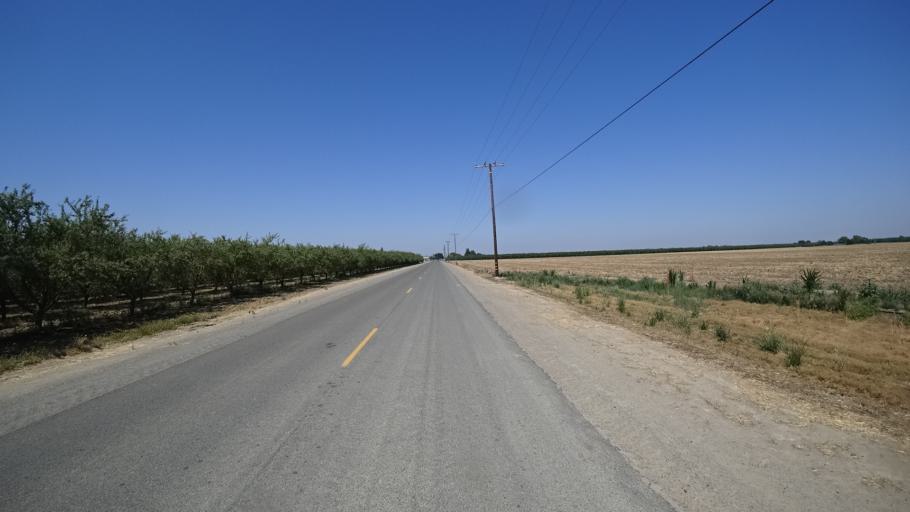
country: US
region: California
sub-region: Kings County
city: Hanford
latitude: 36.3717
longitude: -119.5971
